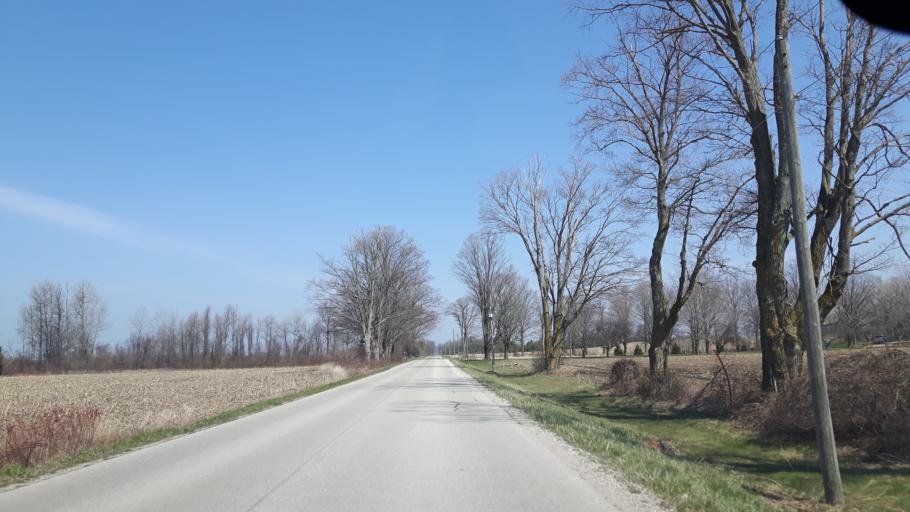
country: CA
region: Ontario
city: Goderich
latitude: 43.6775
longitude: -81.6847
